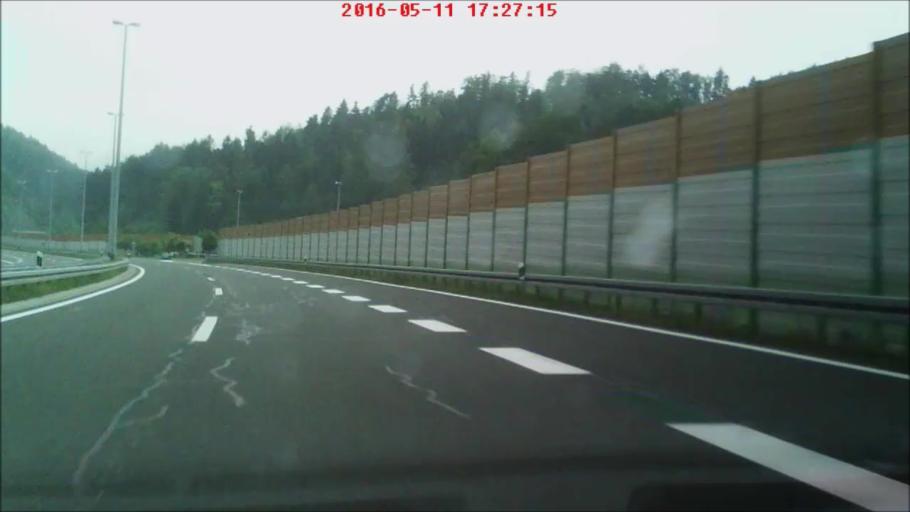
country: SI
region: Zetale
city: Zetale
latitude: 46.2440
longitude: 15.8471
